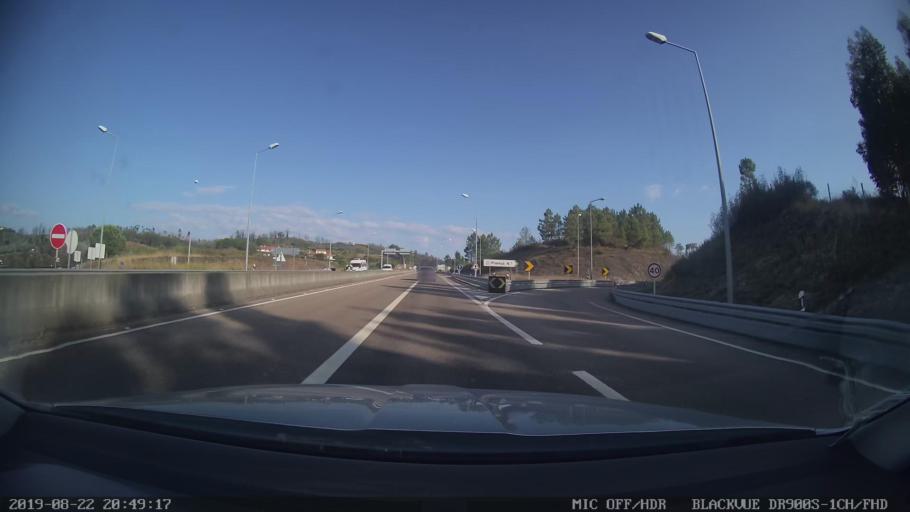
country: PT
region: Castelo Branco
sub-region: Proenca-A-Nova
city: Proenca-a-Nova
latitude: 39.7405
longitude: -7.9264
